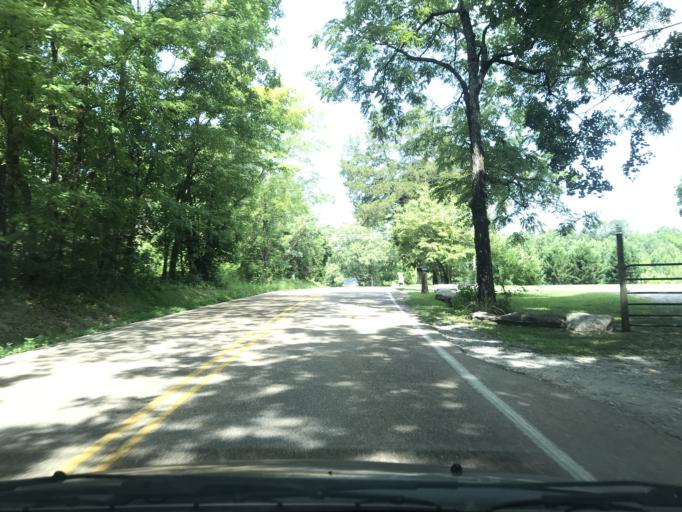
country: US
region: Tennessee
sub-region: Hamilton County
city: Lakesite
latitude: 35.1681
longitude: -85.0711
